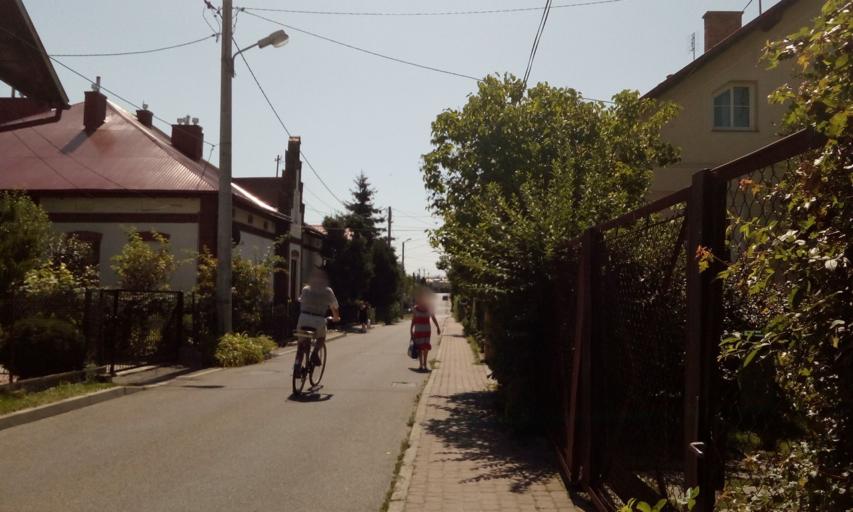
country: PL
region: Subcarpathian Voivodeship
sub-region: Powiat lancucki
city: Lancut
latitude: 50.0643
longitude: 22.2325
